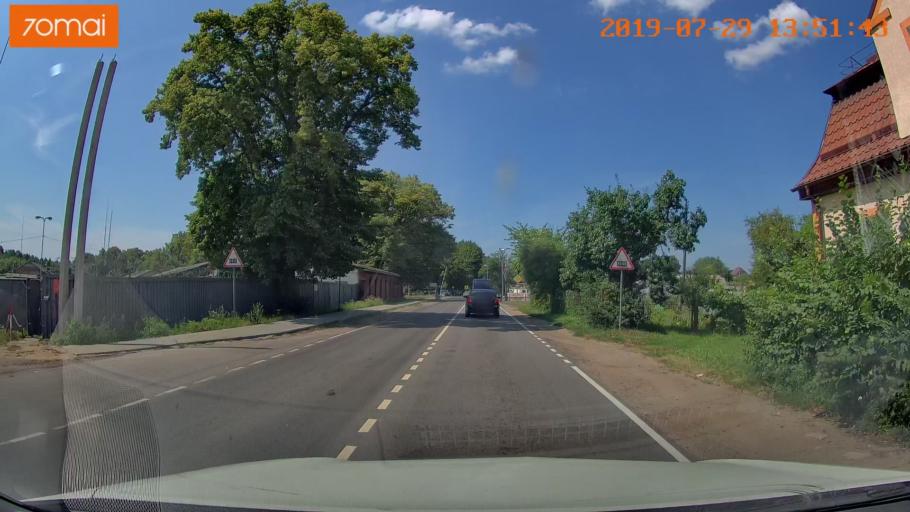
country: RU
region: Kaliningrad
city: Primorsk
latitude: 54.7296
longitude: 19.9999
